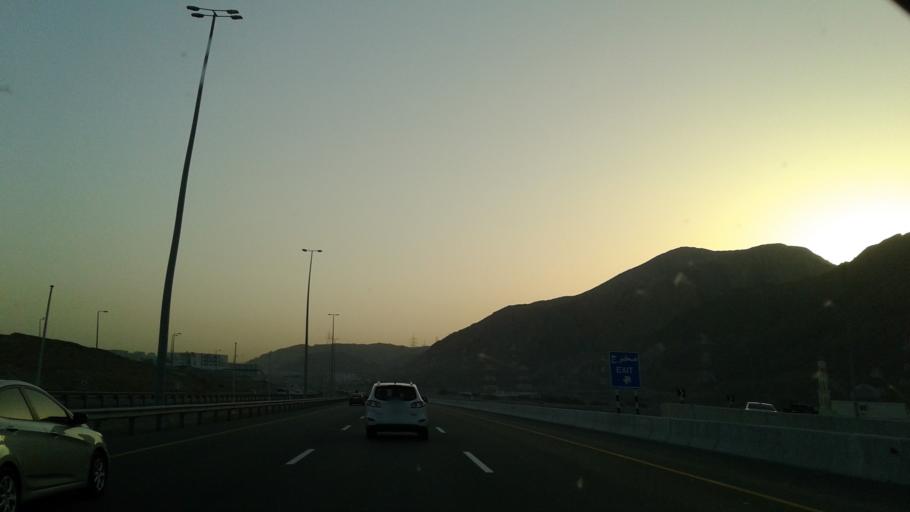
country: OM
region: Muhafazat Masqat
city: Bawshar
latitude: 23.5717
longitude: 58.4259
